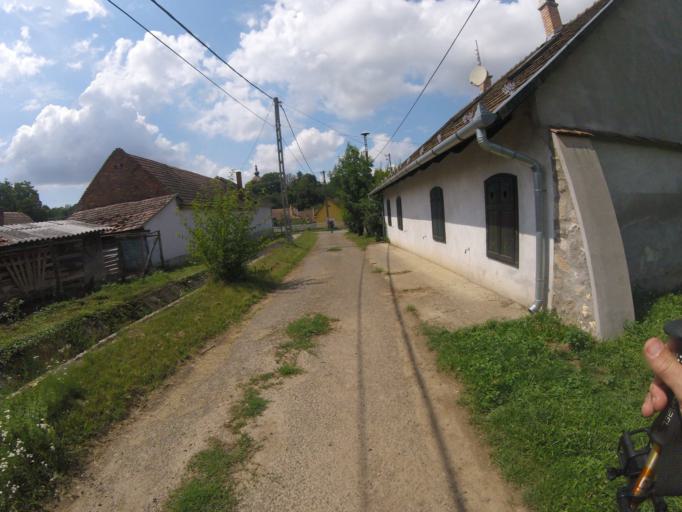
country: SK
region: Nitriansky
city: Sahy
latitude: 48.0356
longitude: 18.9158
